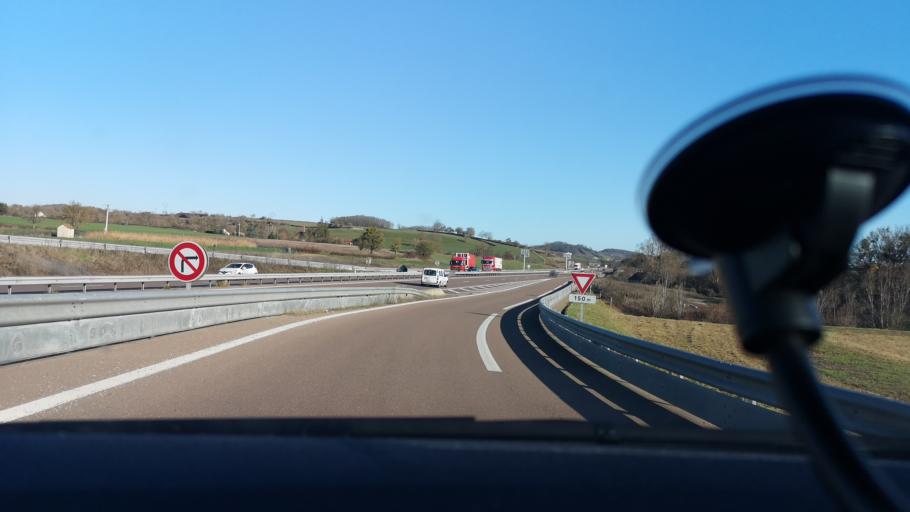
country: FR
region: Bourgogne
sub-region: Departement de Saone-et-Loire
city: Buxy
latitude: 46.7453
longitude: 4.6450
